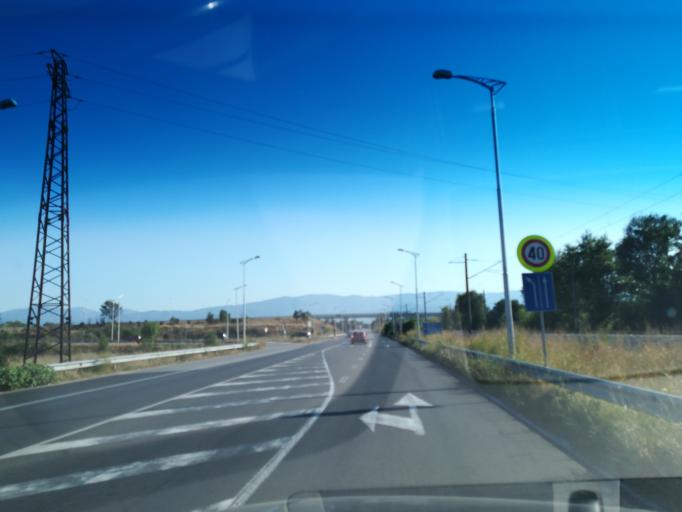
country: BG
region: Plovdiv
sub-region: Obshtina Plovdiv
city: Plovdiv
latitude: 42.1502
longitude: 24.8073
